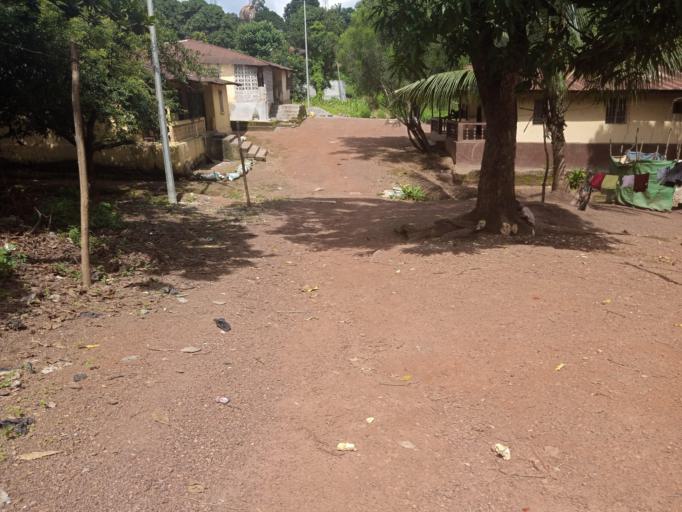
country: SL
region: Northern Province
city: Kamakwie
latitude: 9.4944
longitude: -12.2409
